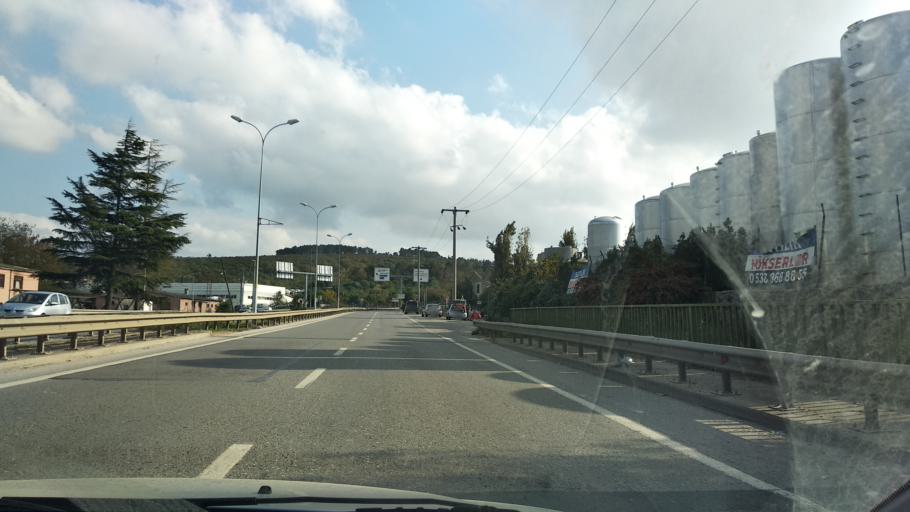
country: TR
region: Istanbul
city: Sultanbeyli
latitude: 40.9316
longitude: 29.3337
